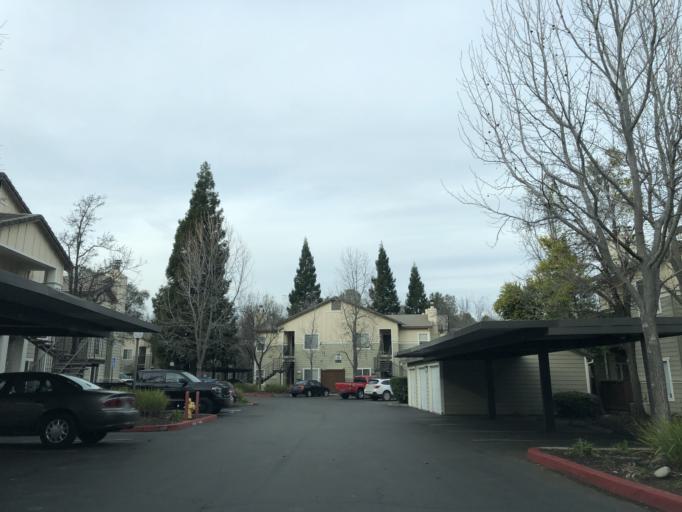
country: US
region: California
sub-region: Sacramento County
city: Folsom
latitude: 38.6496
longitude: -121.1813
